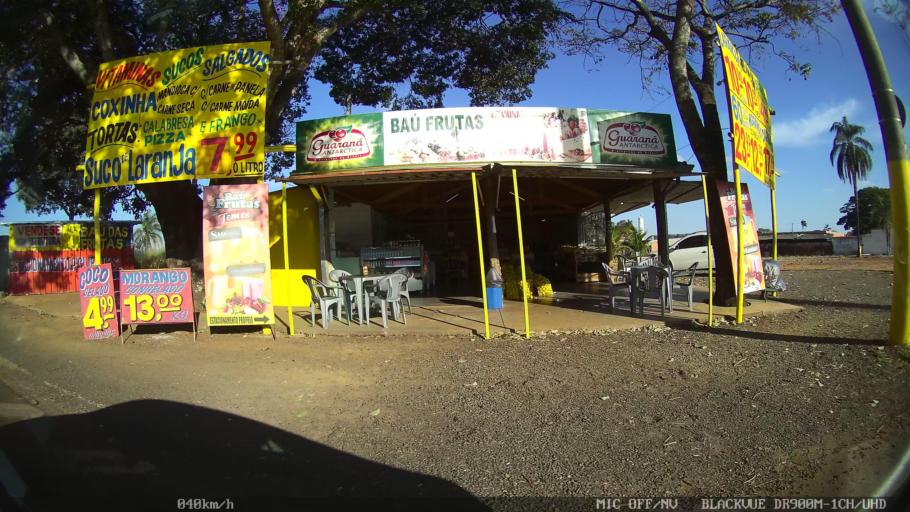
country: BR
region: Sao Paulo
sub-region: Franca
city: Franca
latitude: -20.5150
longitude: -47.3786
